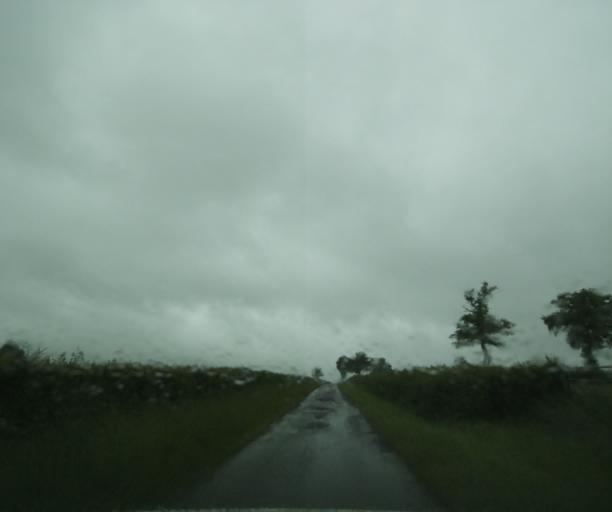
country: FR
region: Bourgogne
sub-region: Departement de Saone-et-Loire
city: Ciry-le-Noble
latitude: 46.5449
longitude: 4.3696
